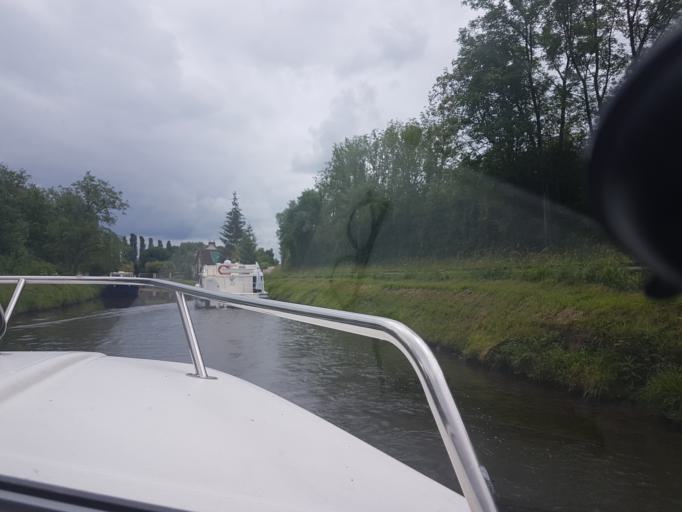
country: FR
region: Bourgogne
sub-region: Departement de l'Yonne
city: Champs-sur-Yonne
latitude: 47.7393
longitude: 3.5907
